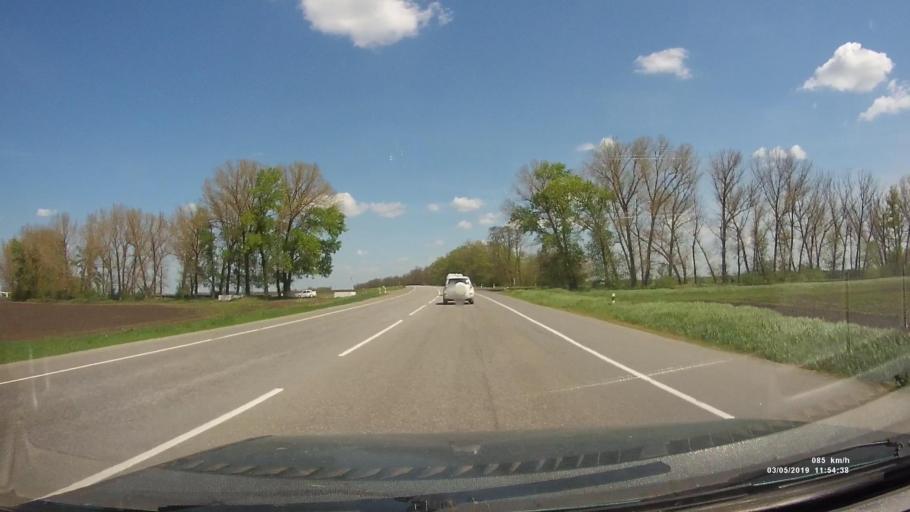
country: RU
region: Rostov
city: Bagayevskaya
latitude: 47.1719
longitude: 40.2830
